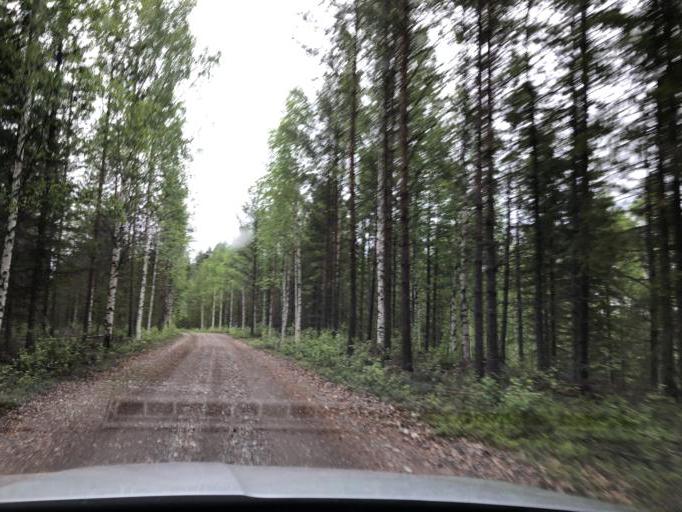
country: SE
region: Norrbotten
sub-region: Pitea Kommun
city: Roknas
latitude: 65.3971
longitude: 21.2647
